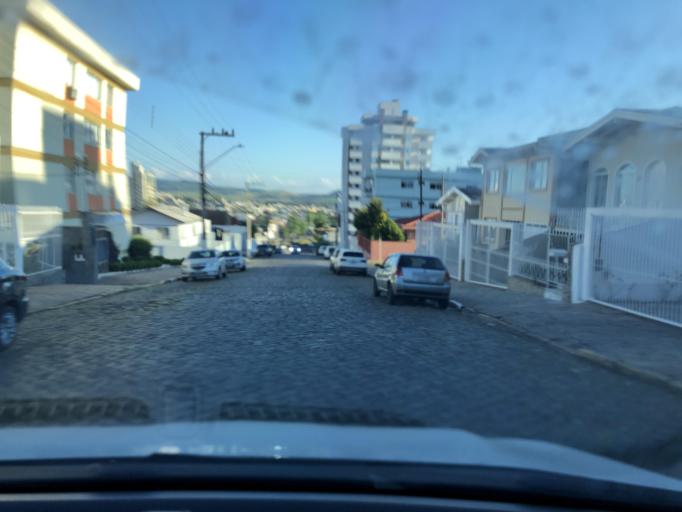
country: BR
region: Santa Catarina
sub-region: Lages
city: Lages
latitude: -27.8202
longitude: -50.3236
